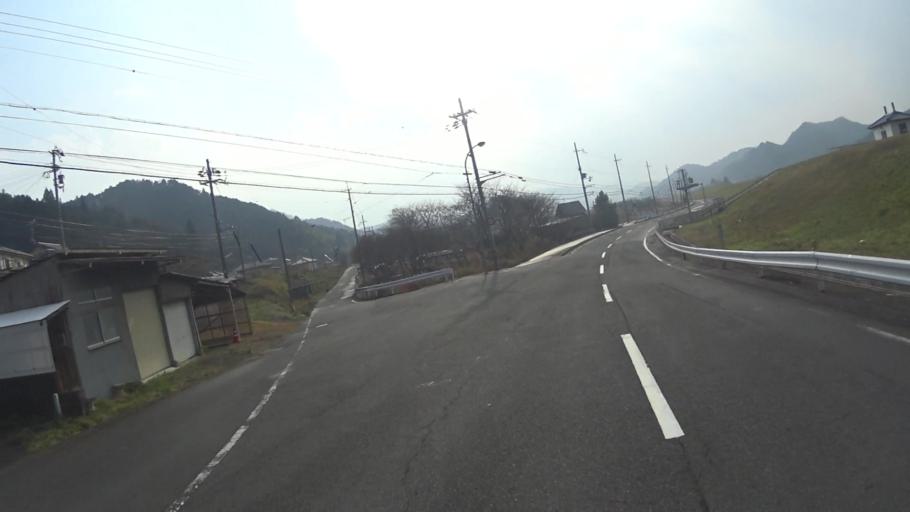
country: JP
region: Kyoto
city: Maizuru
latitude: 35.4797
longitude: 135.2835
